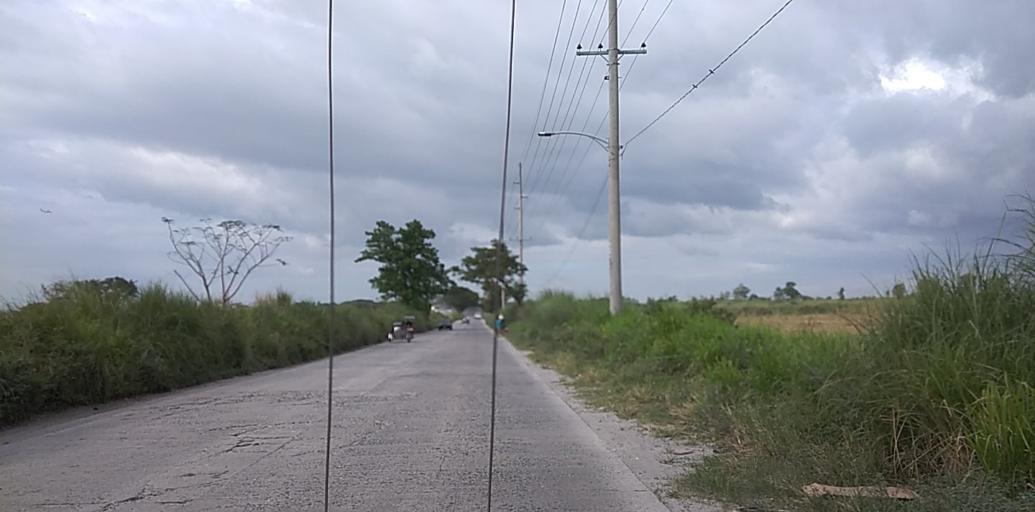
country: PH
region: Central Luzon
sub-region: Province of Pampanga
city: Porac
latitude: 15.0715
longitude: 120.5500
